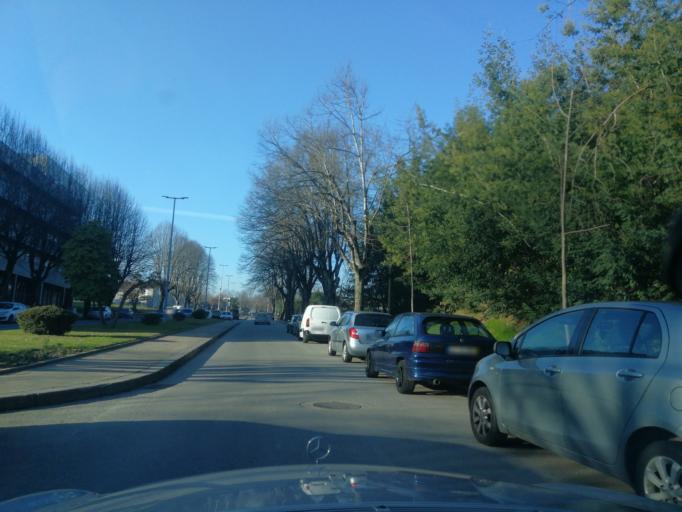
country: PT
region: Braga
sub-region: Guimaraes
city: Ponte
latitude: 41.4838
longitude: -8.3431
